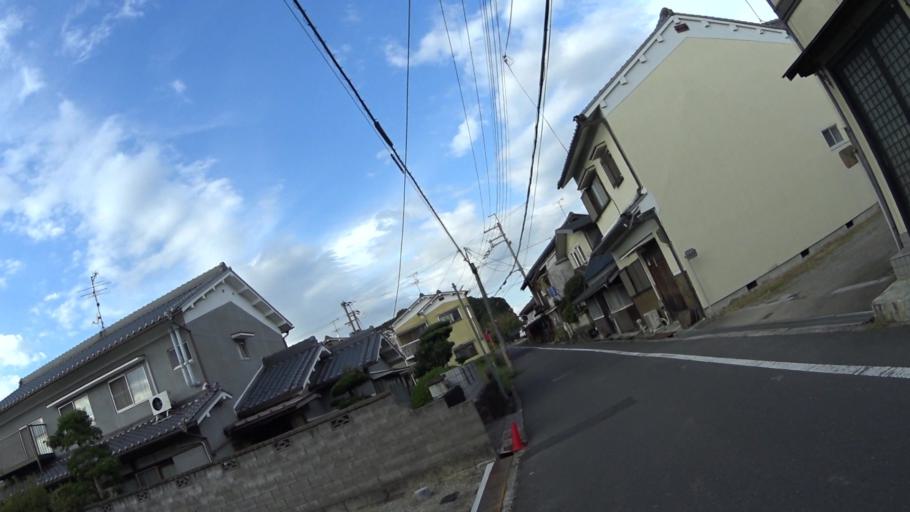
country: JP
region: Nara
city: Sakurai
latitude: 34.5362
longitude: 135.8417
